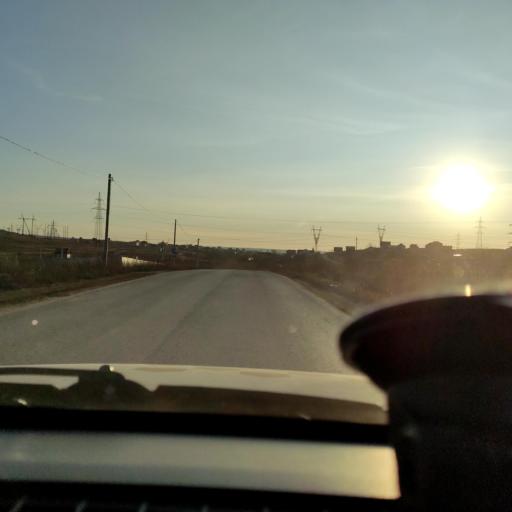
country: RU
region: Perm
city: Ferma
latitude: 57.9532
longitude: 56.3682
